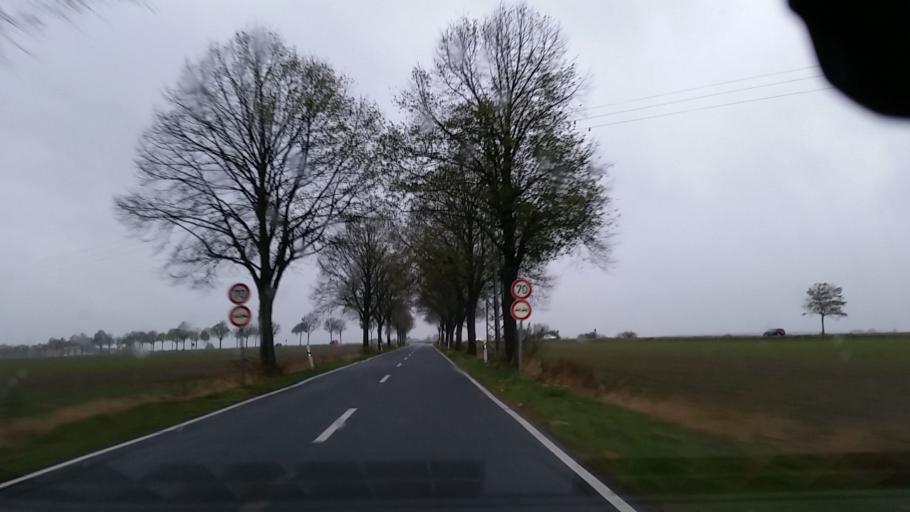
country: DE
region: Lower Saxony
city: Calberlah
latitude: 52.4010
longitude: 10.6639
